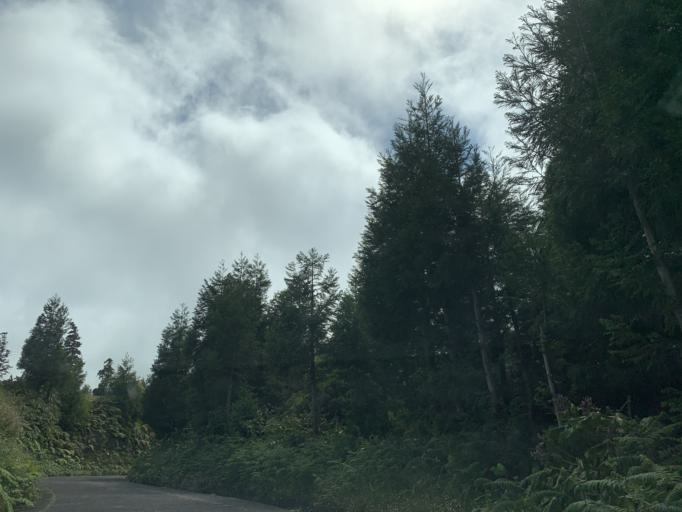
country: PT
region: Azores
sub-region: Ponta Delgada
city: Arrifes
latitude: 37.8501
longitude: -25.7375
